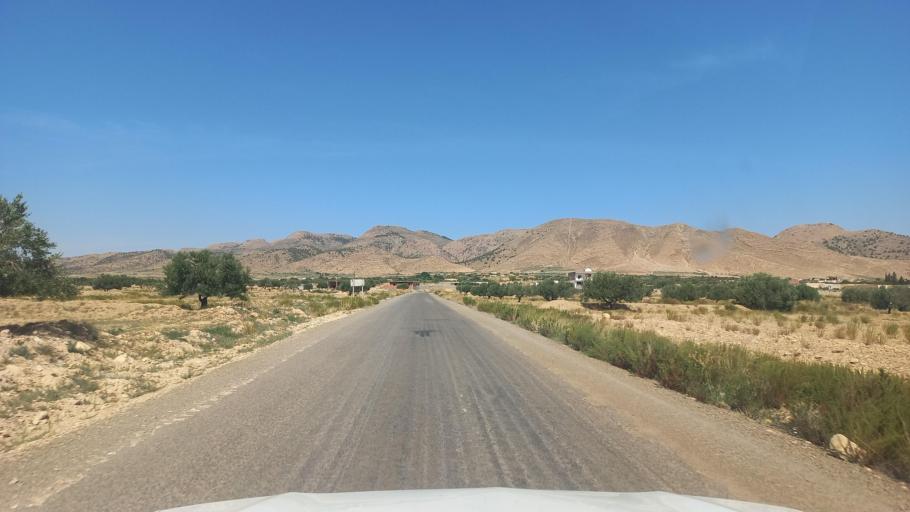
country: TN
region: Al Qasrayn
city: Sbiba
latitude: 35.4402
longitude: 9.0757
